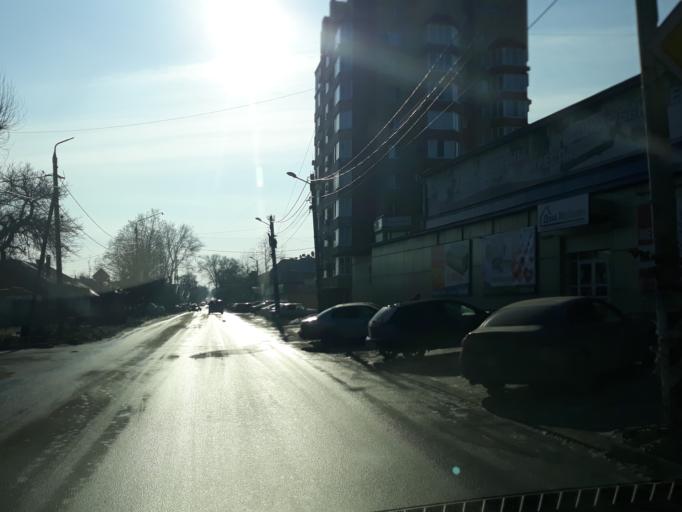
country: RU
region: Rostov
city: Taganrog
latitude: 47.2239
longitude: 38.9119
